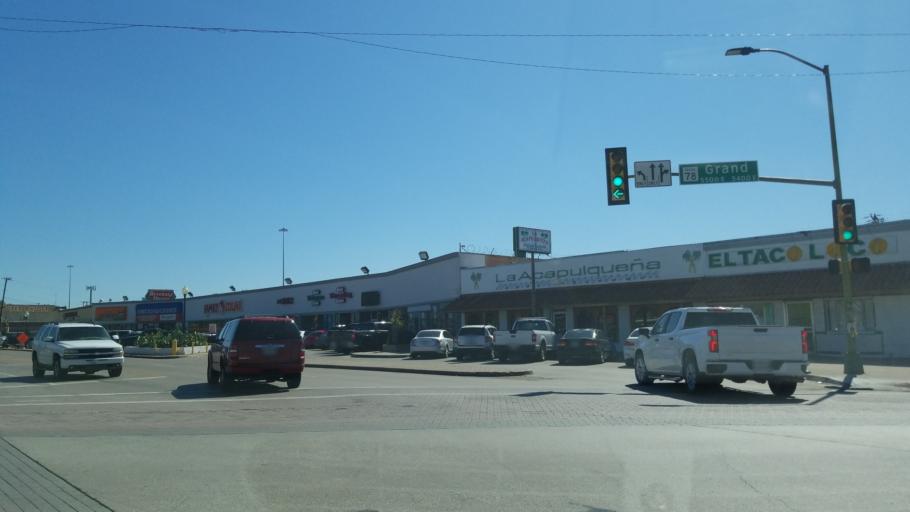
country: US
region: Texas
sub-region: Dallas County
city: Dallas
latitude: 32.7931
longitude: -96.7482
